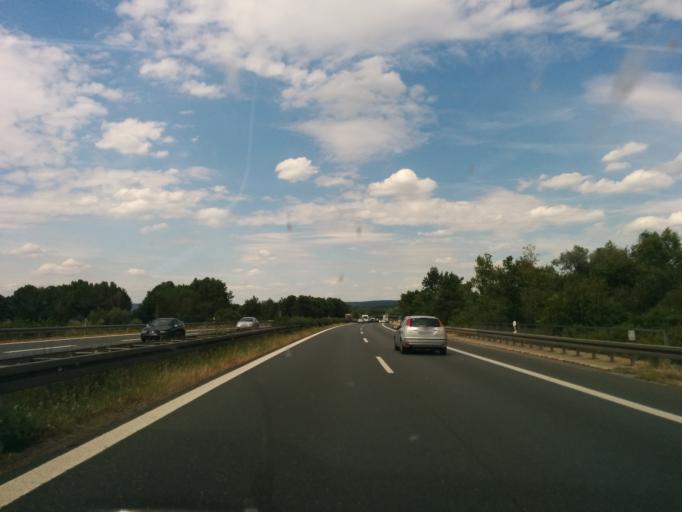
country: DE
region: Bavaria
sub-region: Upper Franconia
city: Forchheim
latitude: 49.7409
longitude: 11.0553
